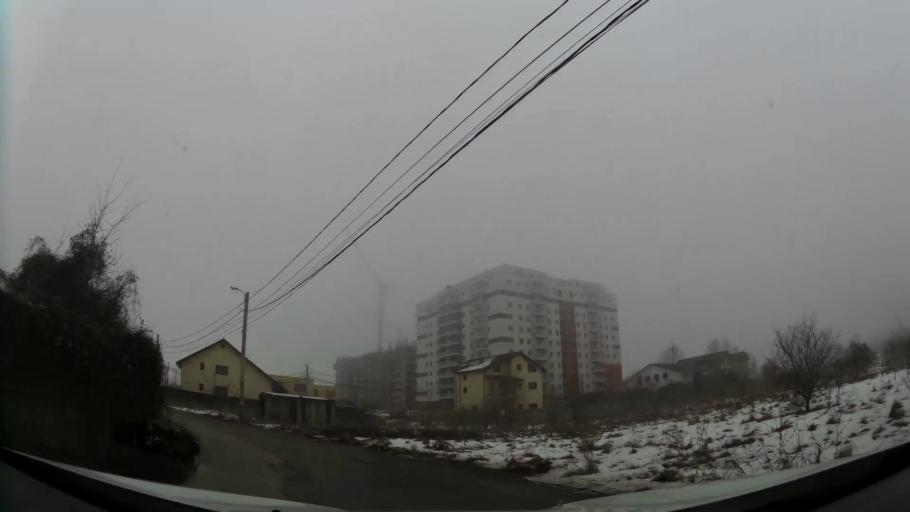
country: RO
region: Ilfov
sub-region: Comuna Chiajna
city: Rosu
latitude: 44.4467
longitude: 26.0208
